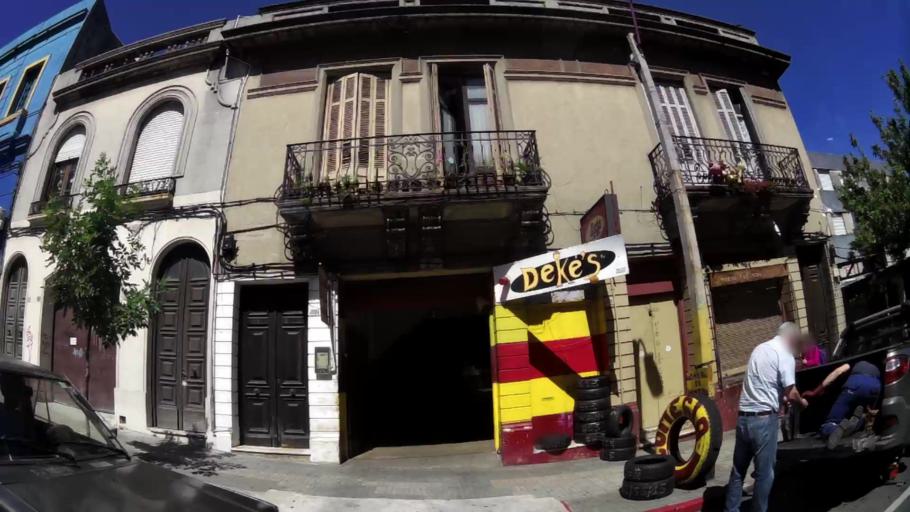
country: UY
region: Montevideo
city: Montevideo
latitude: -34.8992
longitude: -56.1832
